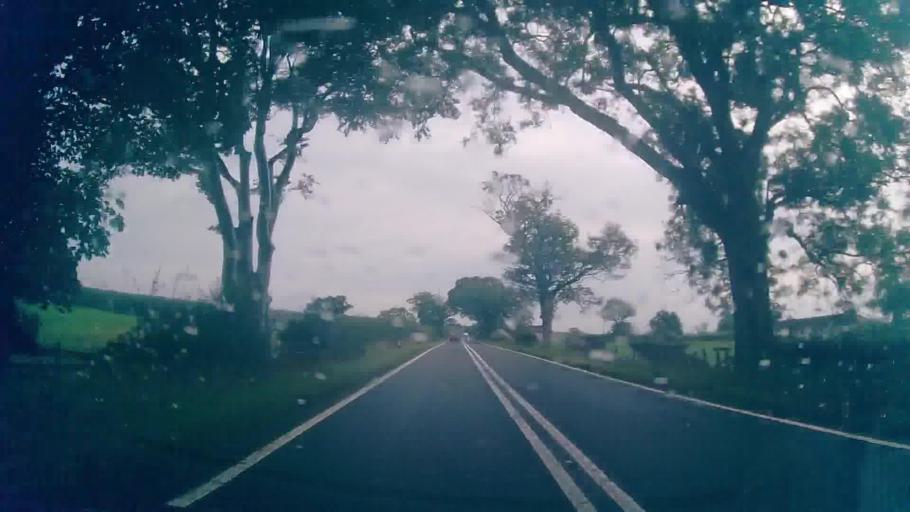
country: GB
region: Scotland
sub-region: Dumfries and Galloway
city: Lochmaben
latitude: 55.0629
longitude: -3.4952
